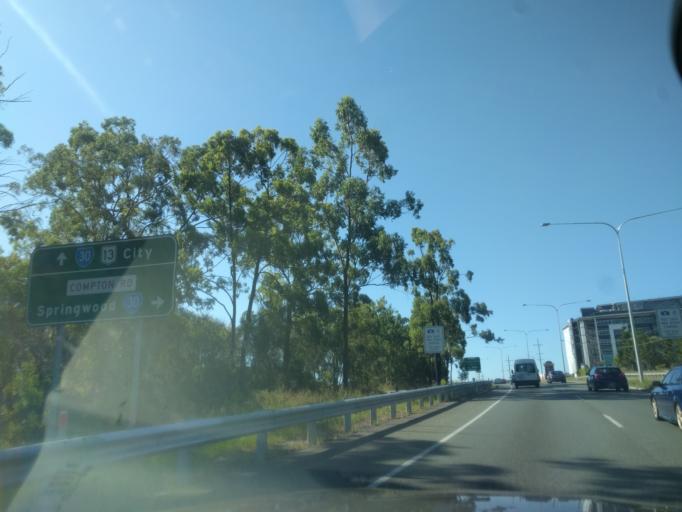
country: AU
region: Queensland
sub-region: Brisbane
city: Sunnybank Hills
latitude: -27.6138
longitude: 153.0516
